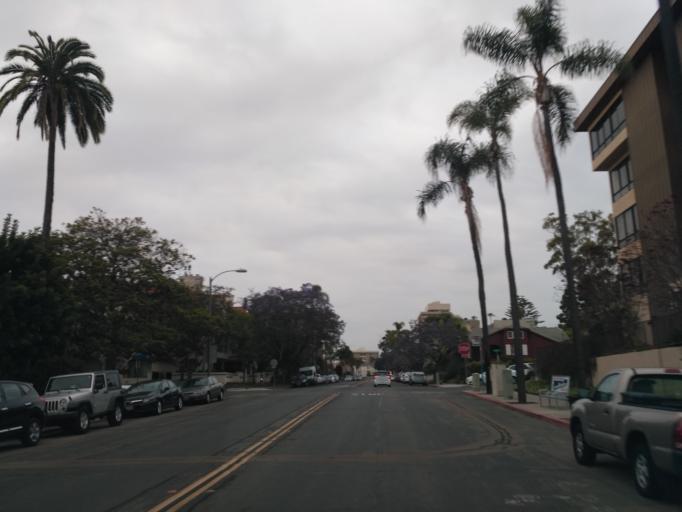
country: US
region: California
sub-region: San Diego County
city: San Diego
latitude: 32.7382
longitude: -117.1640
